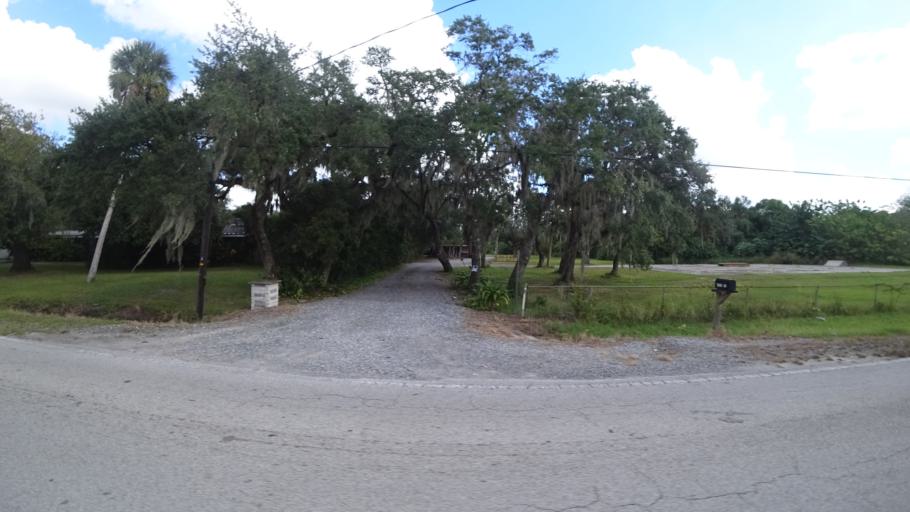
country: US
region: Florida
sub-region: Manatee County
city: Samoset
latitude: 27.4451
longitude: -82.5219
